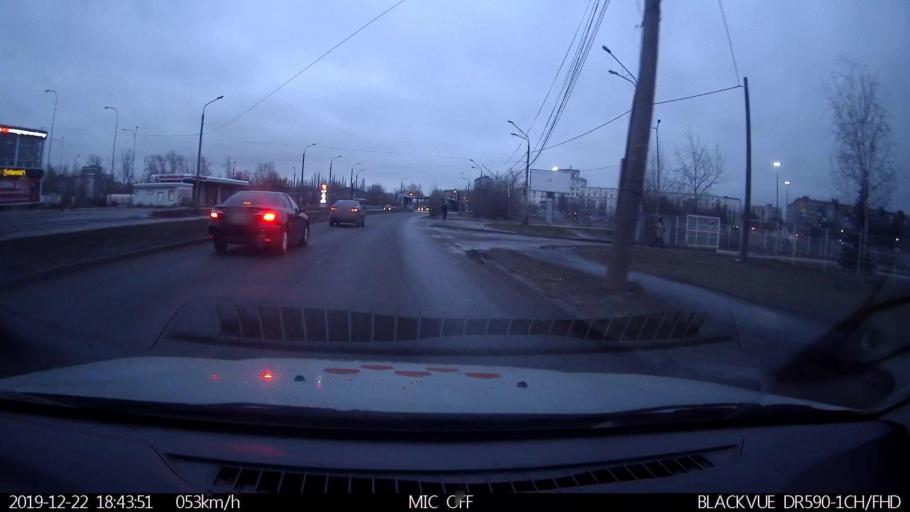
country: RU
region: Nizjnij Novgorod
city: Nizhniy Novgorod
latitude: 56.3391
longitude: 43.8878
